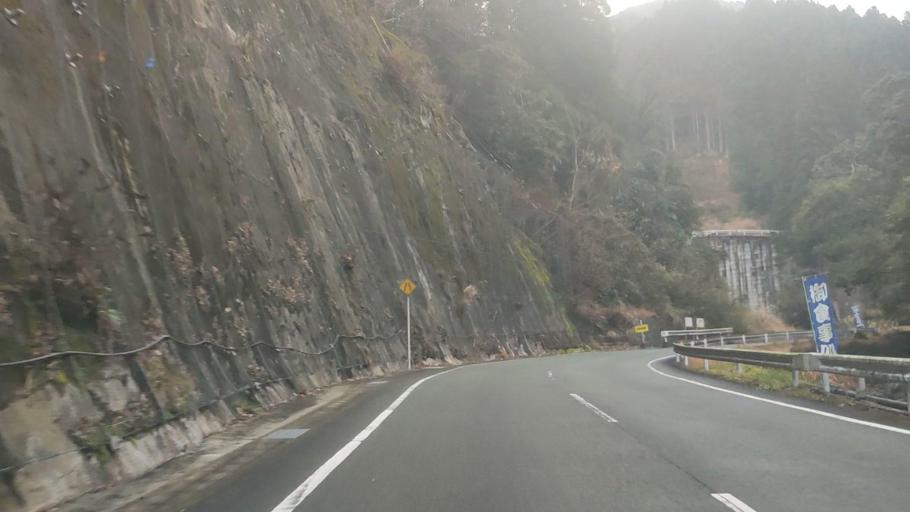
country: JP
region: Kumamoto
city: Matsubase
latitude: 32.5941
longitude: 130.8872
